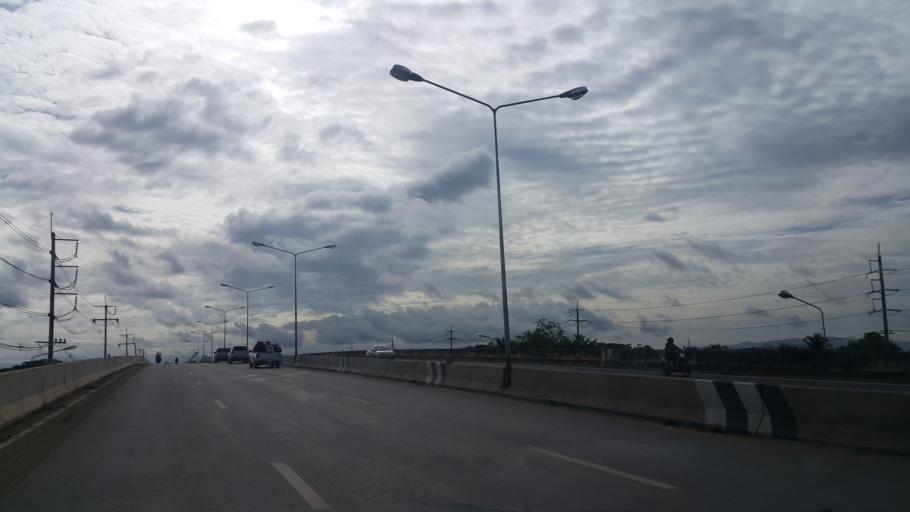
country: TH
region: Chiang Mai
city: Saraphi
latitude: 18.7328
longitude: 99.0301
